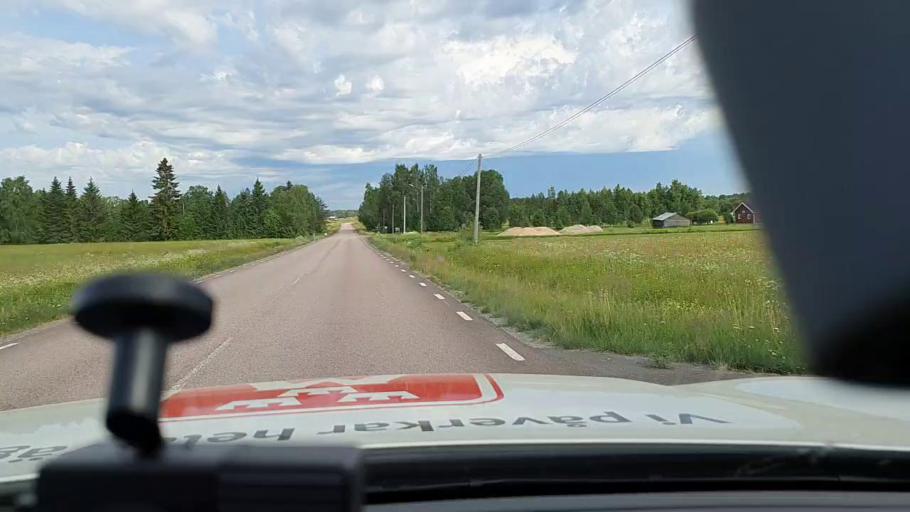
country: SE
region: Norrbotten
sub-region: Bodens Kommun
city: Saevast
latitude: 65.6953
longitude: 21.7793
